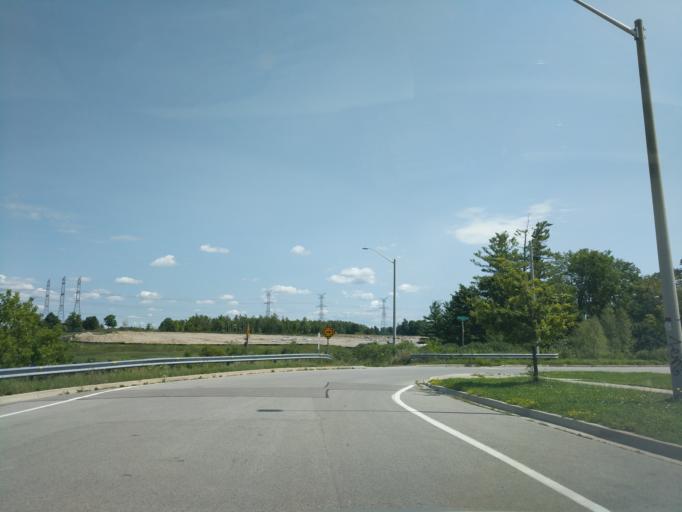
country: CA
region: Ontario
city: Markham
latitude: 43.8476
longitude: -79.2462
